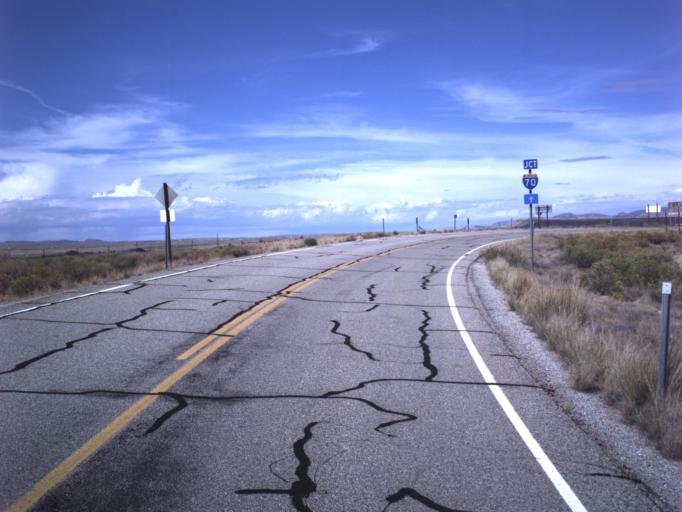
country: US
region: Utah
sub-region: Grand County
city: Moab
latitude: 38.9367
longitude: -109.4052
